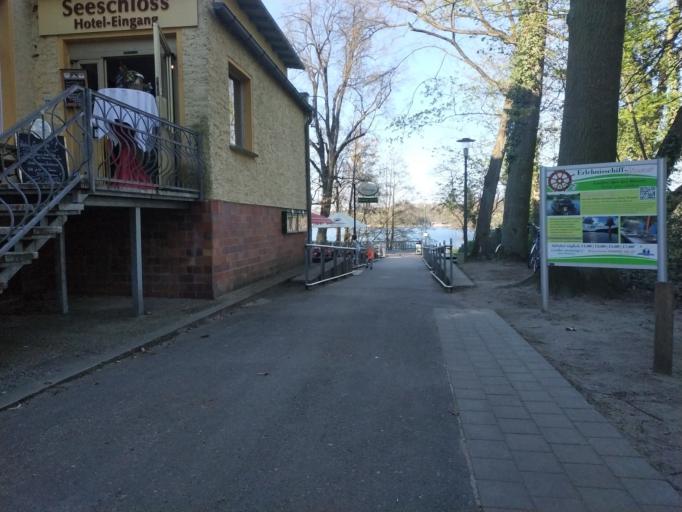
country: DE
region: Brandenburg
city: Petershagen
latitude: 52.5573
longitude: 13.8306
